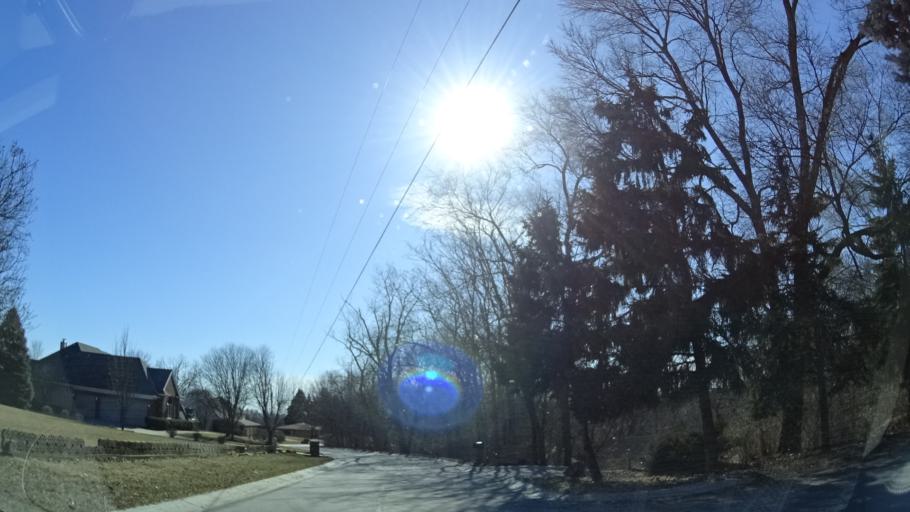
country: US
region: Nebraska
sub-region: Sarpy County
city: Bellevue
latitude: 41.1566
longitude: -95.8917
